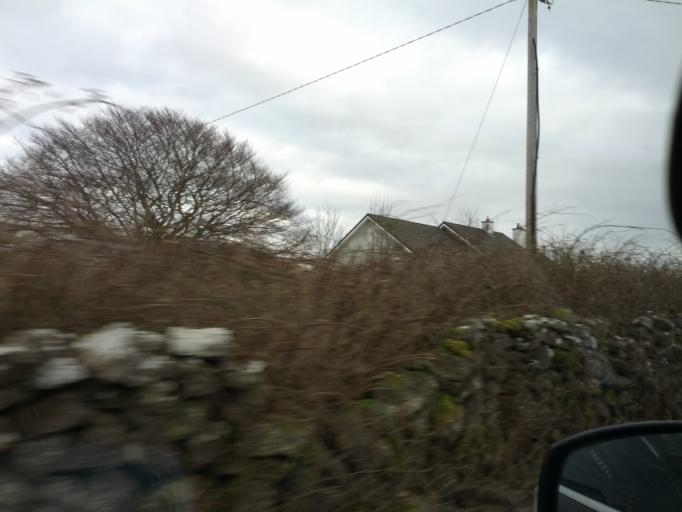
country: IE
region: Connaught
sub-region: County Galway
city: Oranmore
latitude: 53.1645
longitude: -8.8785
